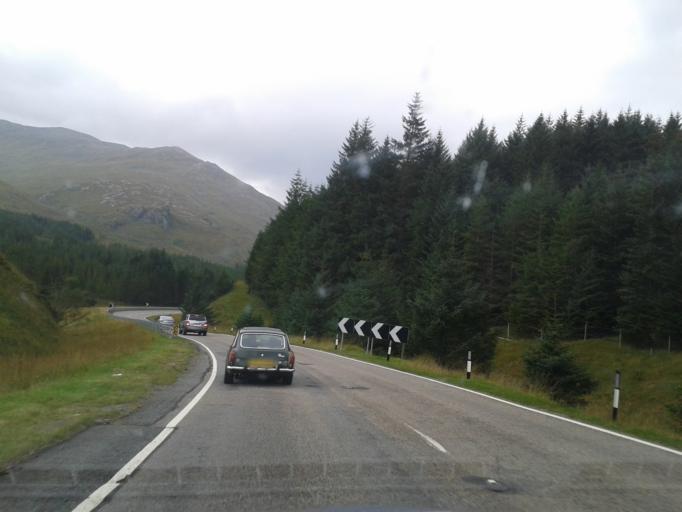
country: GB
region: Scotland
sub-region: Highland
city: Fort William
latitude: 57.1566
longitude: -5.2516
